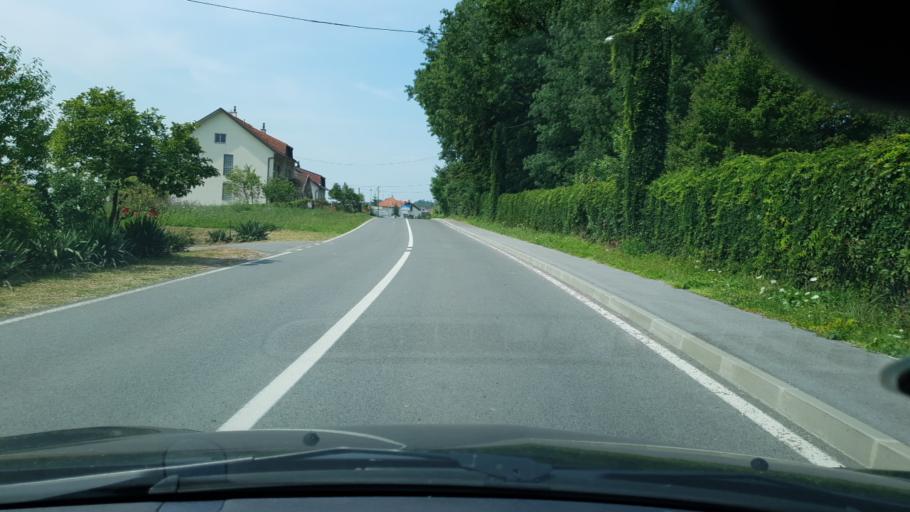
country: HR
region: Krapinsko-Zagorska
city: Bedekovcina
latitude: 46.0354
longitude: 15.9757
